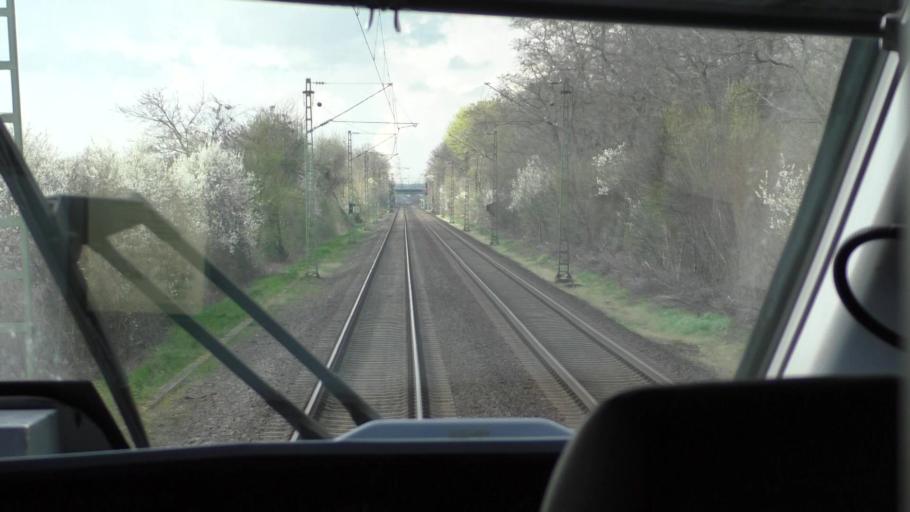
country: DE
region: North Rhine-Westphalia
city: Bornheim
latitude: 50.7843
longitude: 6.9738
